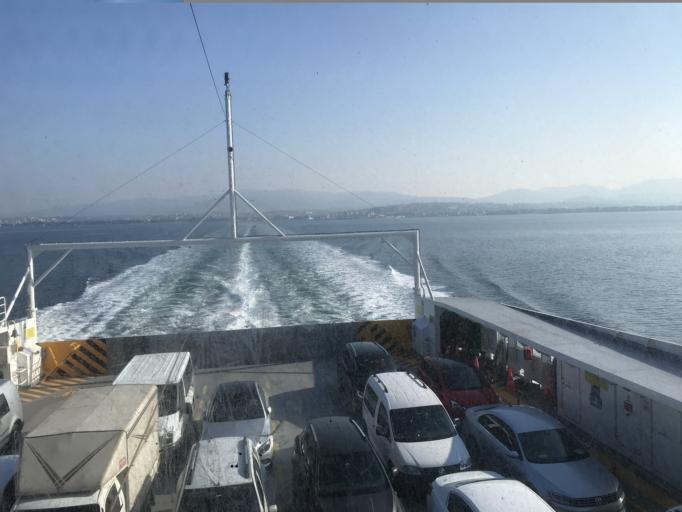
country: TR
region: Yalova
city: Yalova
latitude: 40.6830
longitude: 29.2630
